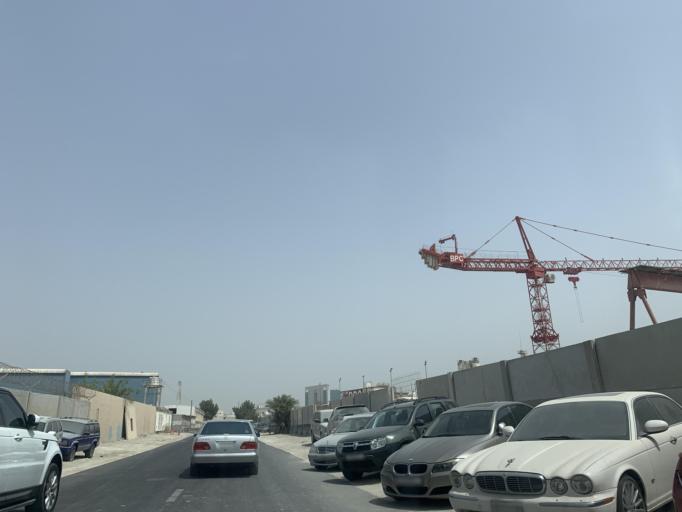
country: BH
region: Northern
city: Madinat `Isa
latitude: 26.1921
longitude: 50.5302
